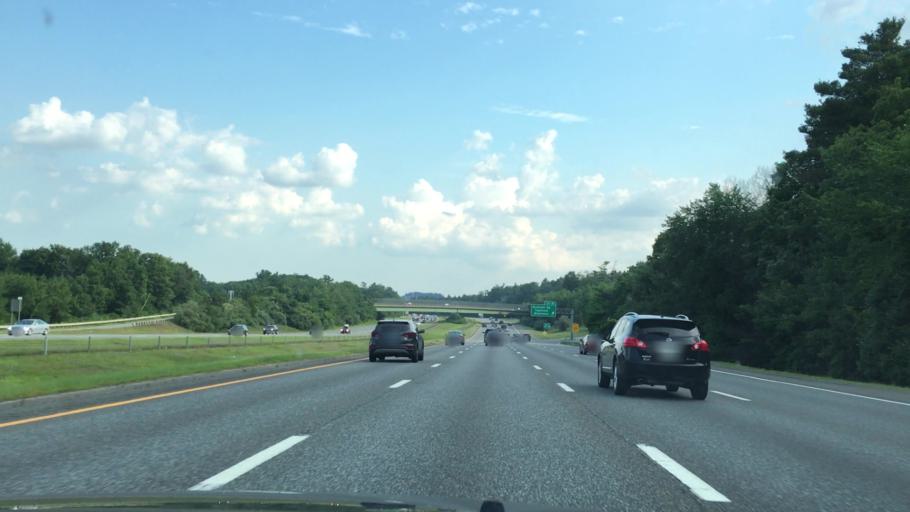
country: US
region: Massachusetts
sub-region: Essex County
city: Topsfield
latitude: 42.6303
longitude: -70.9783
